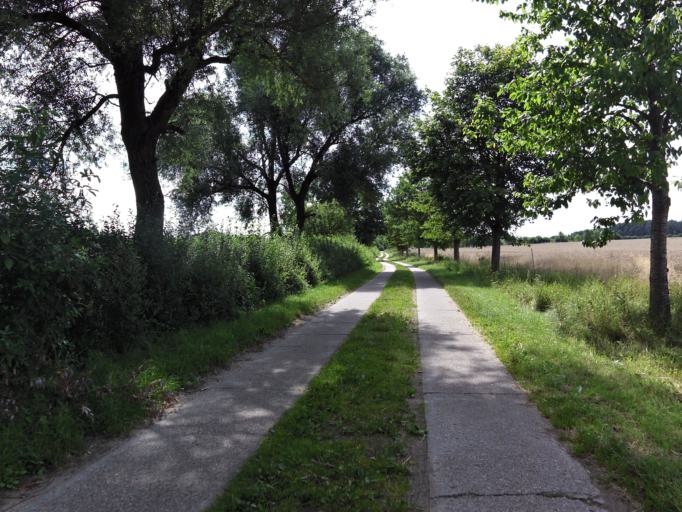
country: DE
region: Brandenburg
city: Lychen
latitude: 53.2745
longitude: 13.3780
